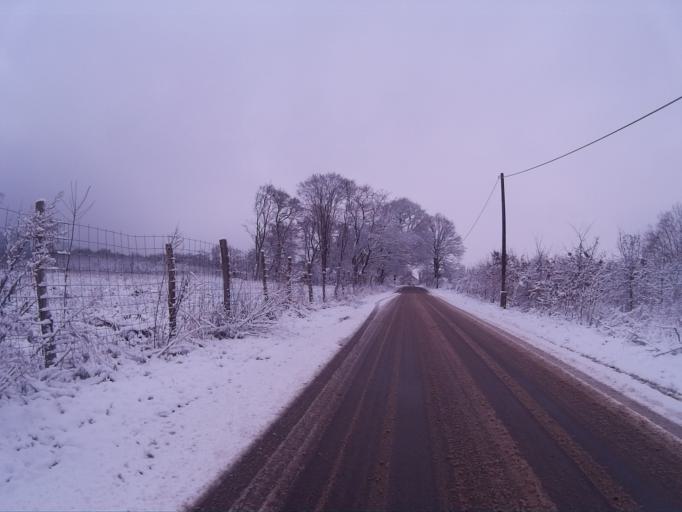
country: HU
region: Komarom-Esztergom
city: Tarjan
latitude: 47.5747
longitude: 18.4969
